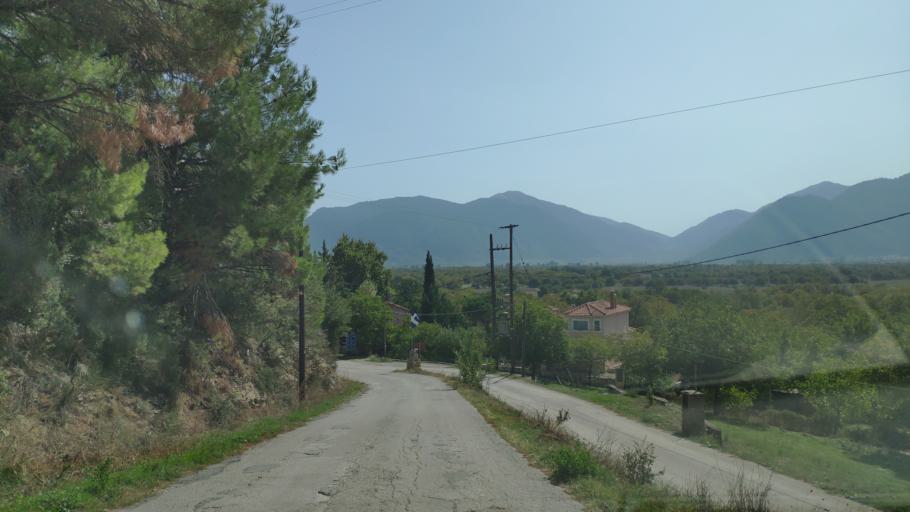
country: GR
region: West Greece
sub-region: Nomos Achaias
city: Kalavryta
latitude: 37.9138
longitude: 22.2999
